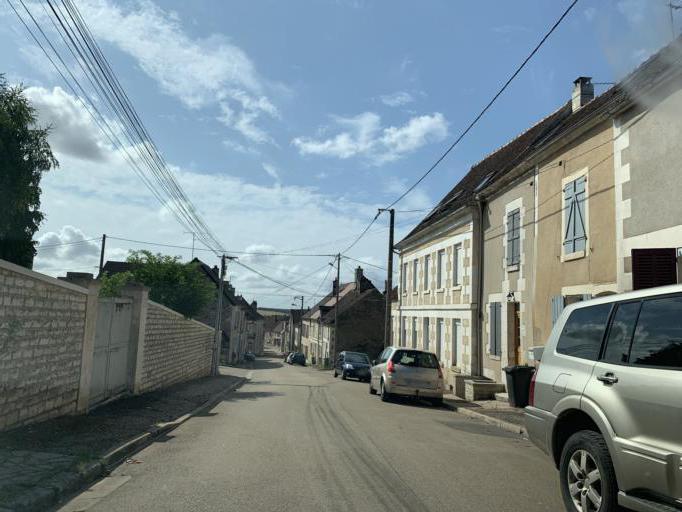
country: FR
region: Bourgogne
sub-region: Departement de l'Yonne
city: Fontenailles
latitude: 47.6168
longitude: 3.4998
